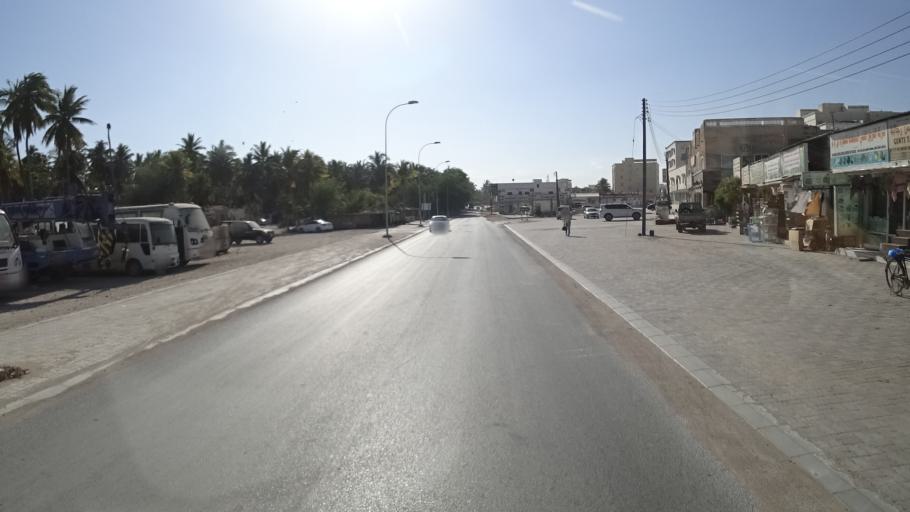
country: OM
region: Zufar
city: Salalah
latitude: 17.0100
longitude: 54.1023
